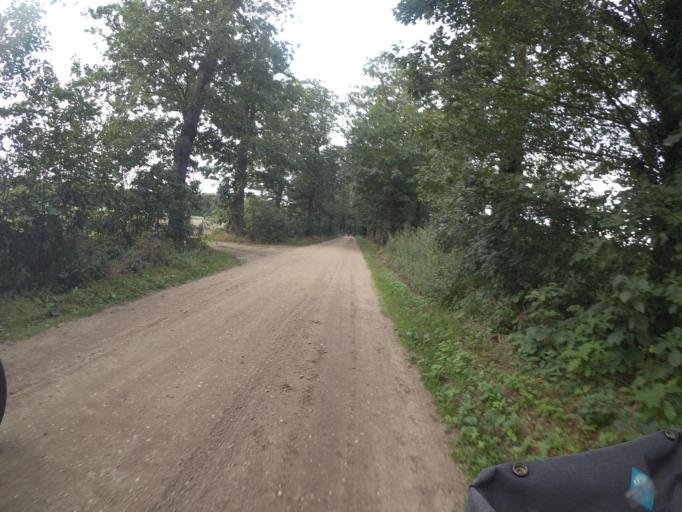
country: NL
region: Limburg
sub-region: Gemeente Gennep
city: Gennep
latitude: 51.6380
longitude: 6.0521
